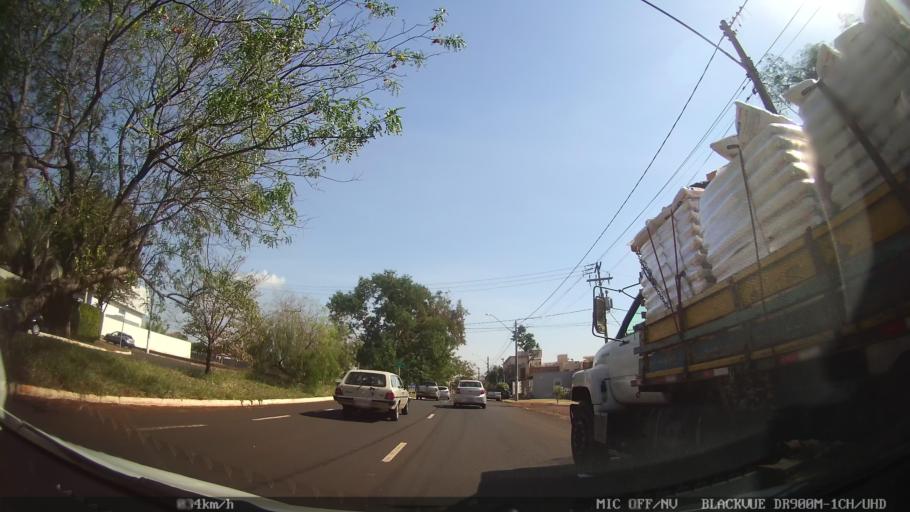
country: BR
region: Sao Paulo
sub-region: Ribeirao Preto
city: Ribeirao Preto
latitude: -21.2041
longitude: -47.8226
